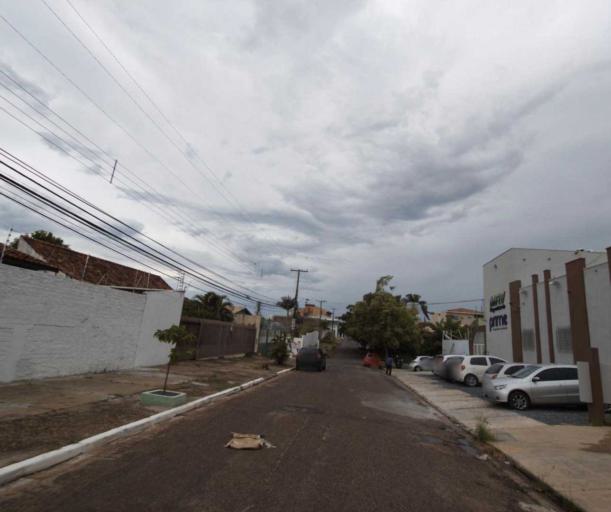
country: BR
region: Mato Grosso
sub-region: Cuiaba
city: Cuiaba
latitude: -15.6050
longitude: -56.0826
